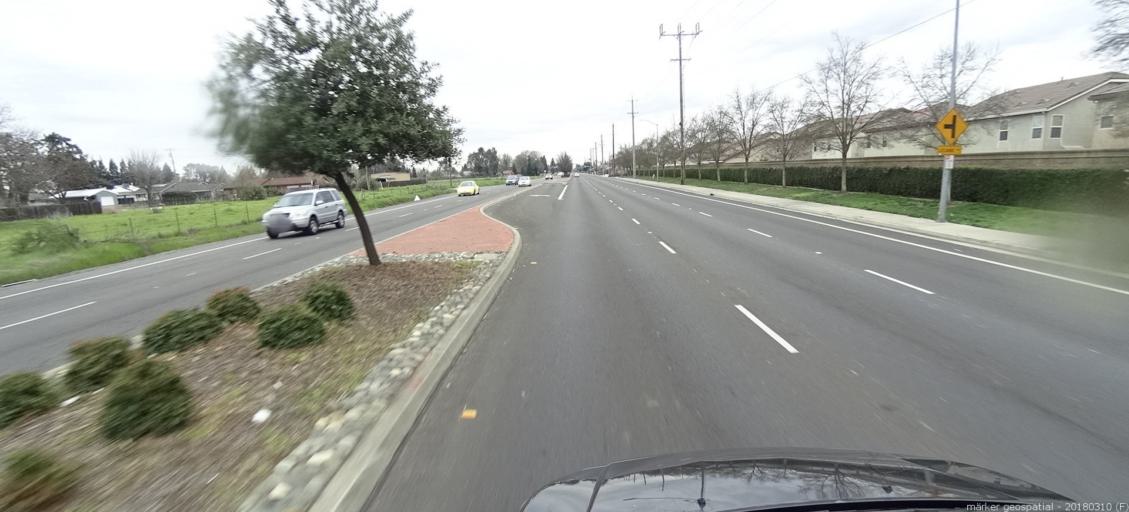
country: US
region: California
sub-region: Sacramento County
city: Vineyard
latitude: 38.4762
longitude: -121.3719
